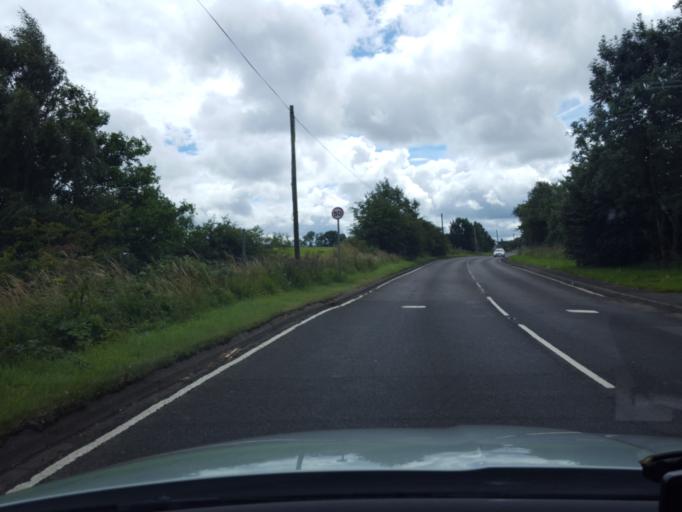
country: GB
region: Scotland
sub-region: Stirling
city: Cowie
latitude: 56.0502
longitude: -3.8580
